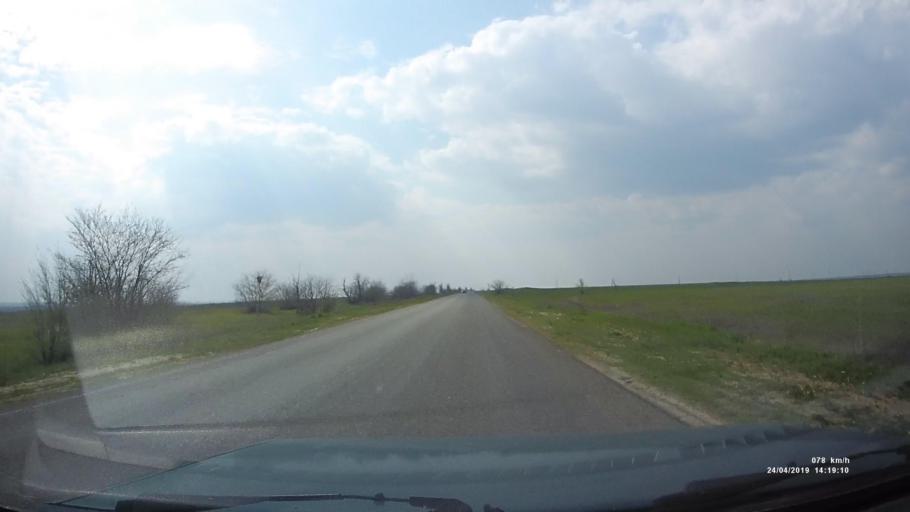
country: RU
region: Kalmykiya
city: Arshan'
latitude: 46.3046
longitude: 44.1805
